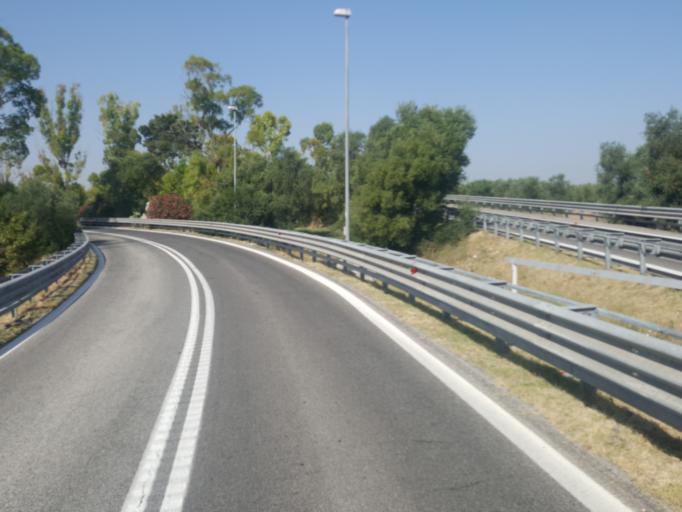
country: IT
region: Apulia
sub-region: Provincia di Bari
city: Molfetta
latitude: 41.1775
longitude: 16.5749
